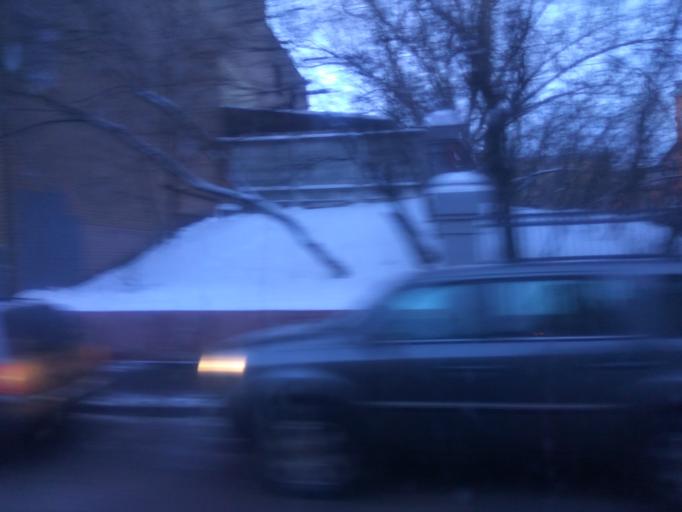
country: RU
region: Moscow
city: Taganskiy
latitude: 55.7312
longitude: 37.6799
